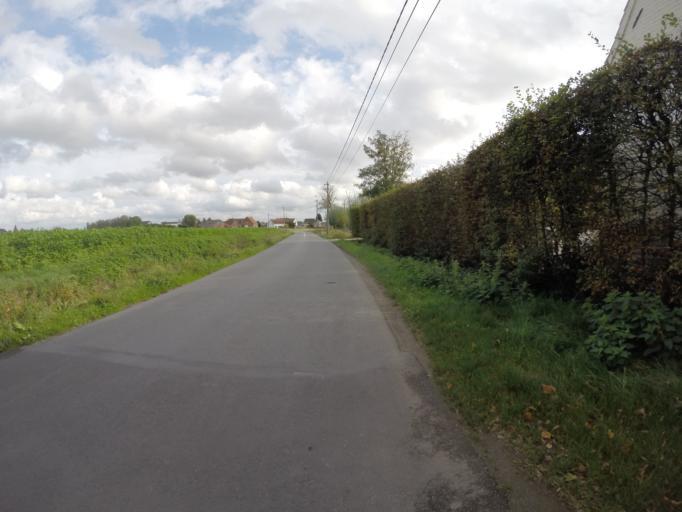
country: BE
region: Flanders
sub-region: Provincie Oost-Vlaanderen
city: Aalter
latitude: 51.0770
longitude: 3.4161
